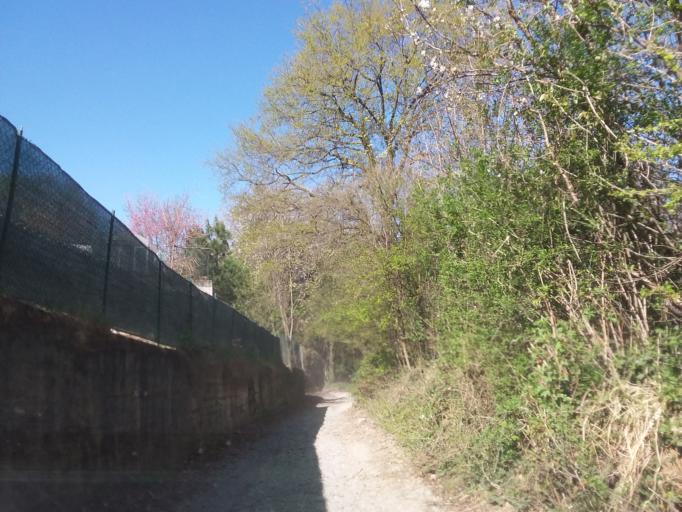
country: IT
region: Piedmont
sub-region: Provincia di Torino
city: Rivoli
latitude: 45.0668
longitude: 7.4967
